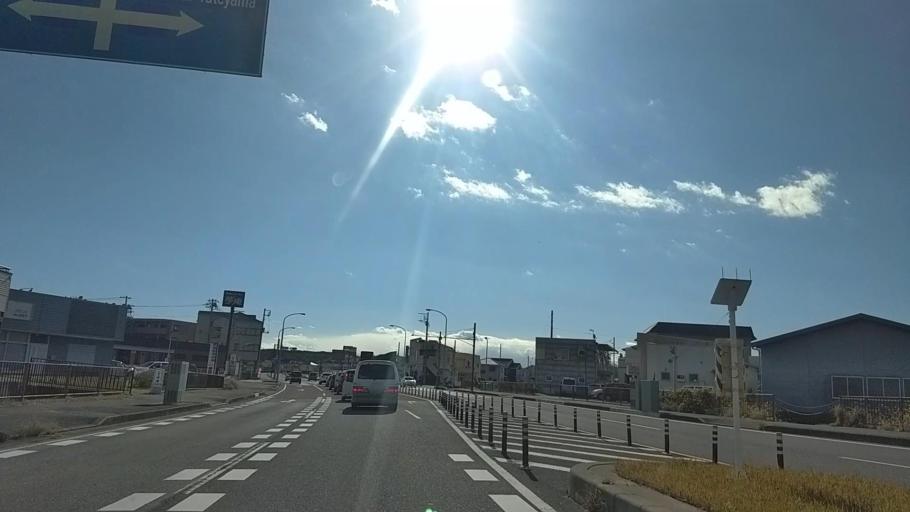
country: JP
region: Chiba
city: Tateyama
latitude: 35.0008
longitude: 139.8720
